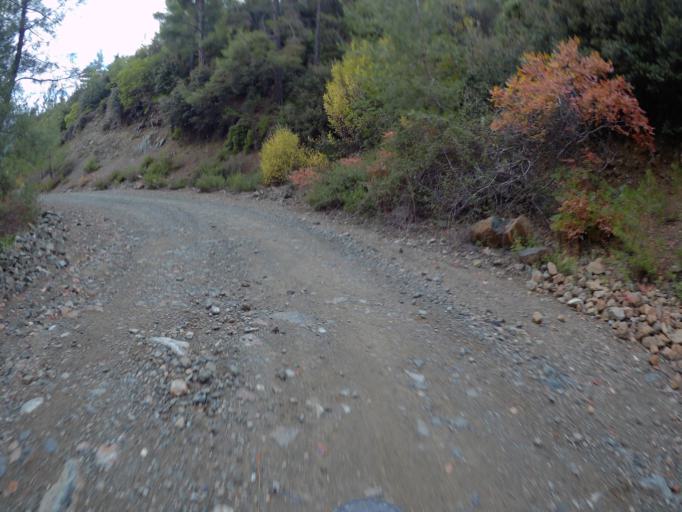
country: CY
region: Lefkosia
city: Kakopetria
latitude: 34.8976
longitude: 32.8485
